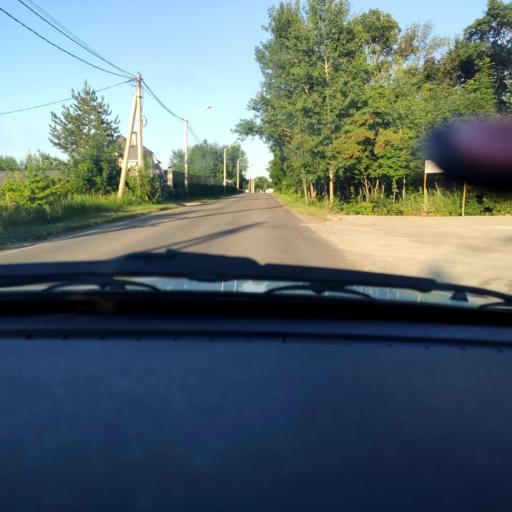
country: RU
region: Voronezj
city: Ramon'
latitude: 51.8903
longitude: 39.2655
